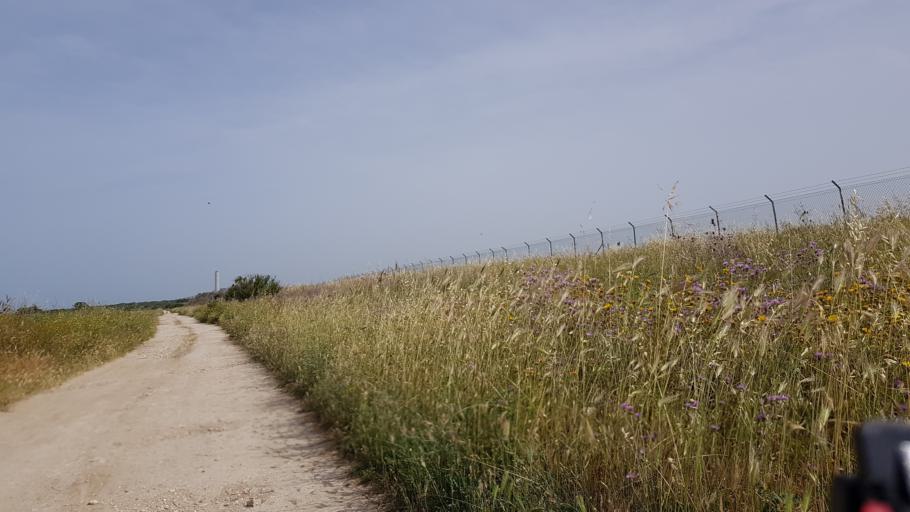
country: IT
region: Apulia
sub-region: Provincia di Brindisi
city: La Rosa
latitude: 40.5946
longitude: 17.9942
